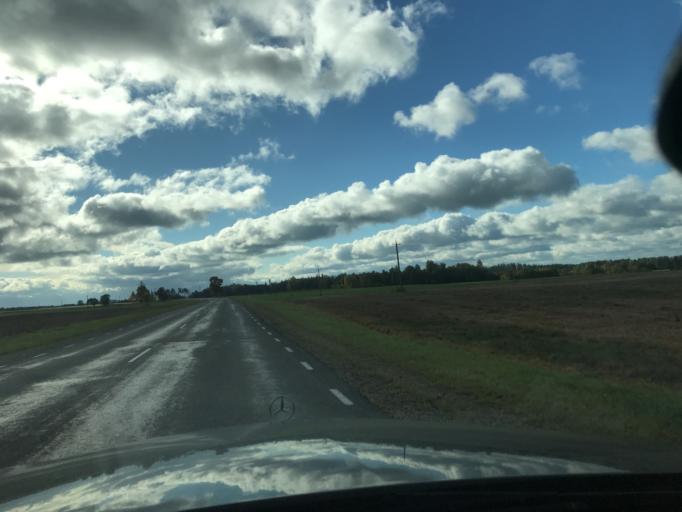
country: EE
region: Valgamaa
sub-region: Valga linn
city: Valga
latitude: 57.9766
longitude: 26.2607
